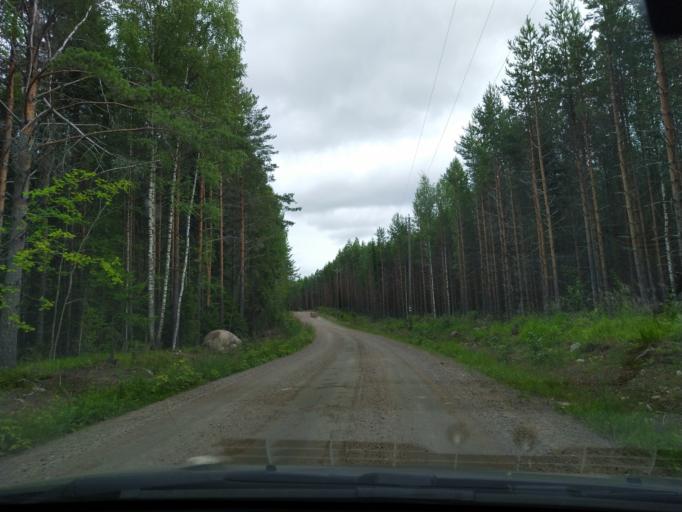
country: FI
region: Southern Savonia
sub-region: Mikkeli
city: Maentyharju
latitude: 61.1409
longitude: 26.8898
